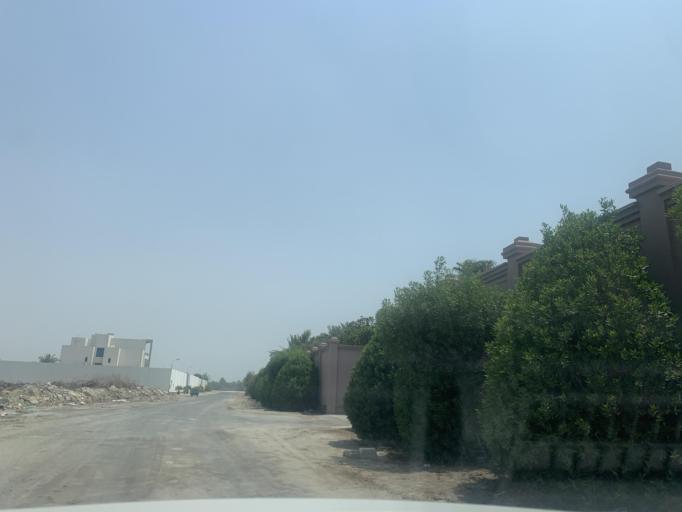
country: BH
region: Central Governorate
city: Madinat Hamad
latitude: 26.1207
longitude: 50.4655
